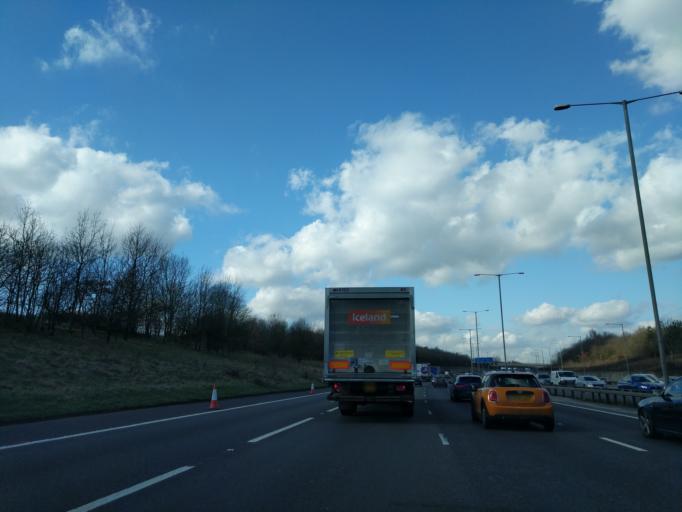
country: GB
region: England
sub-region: Buckinghamshire
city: Denham
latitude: 51.5484
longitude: -0.5194
